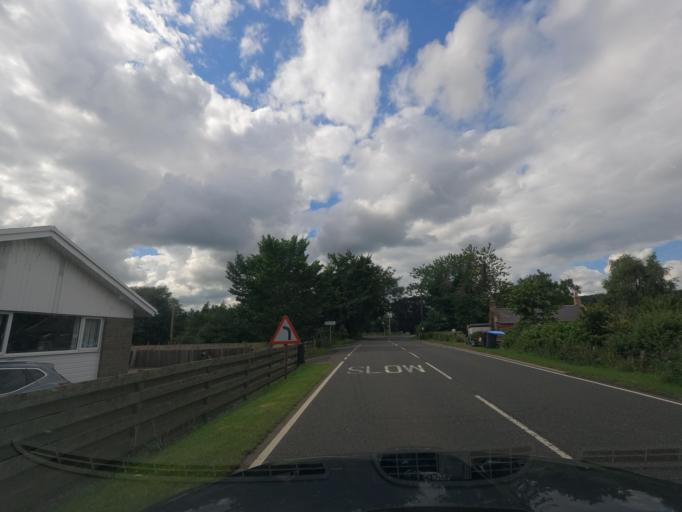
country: GB
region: Scotland
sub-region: The Scottish Borders
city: Kelso
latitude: 55.7058
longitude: -2.4542
